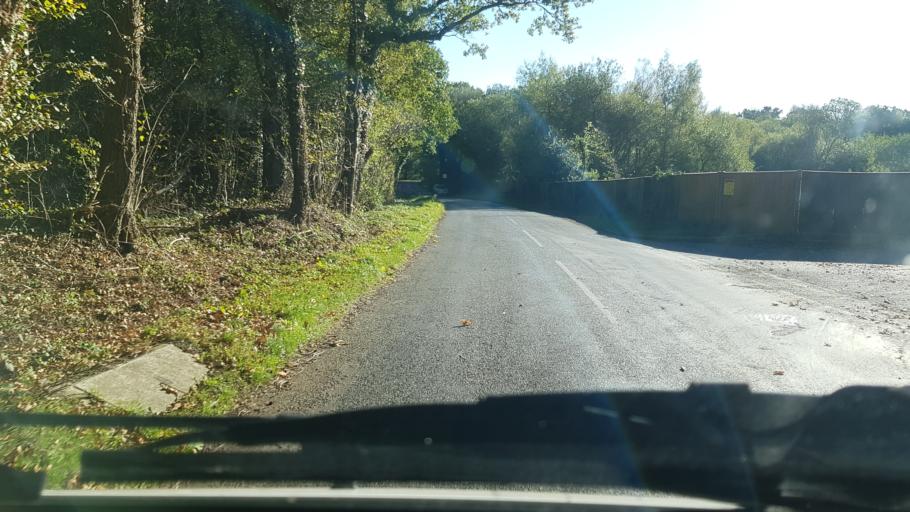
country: GB
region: England
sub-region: Surrey
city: Ockley
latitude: 51.1327
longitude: -0.4170
